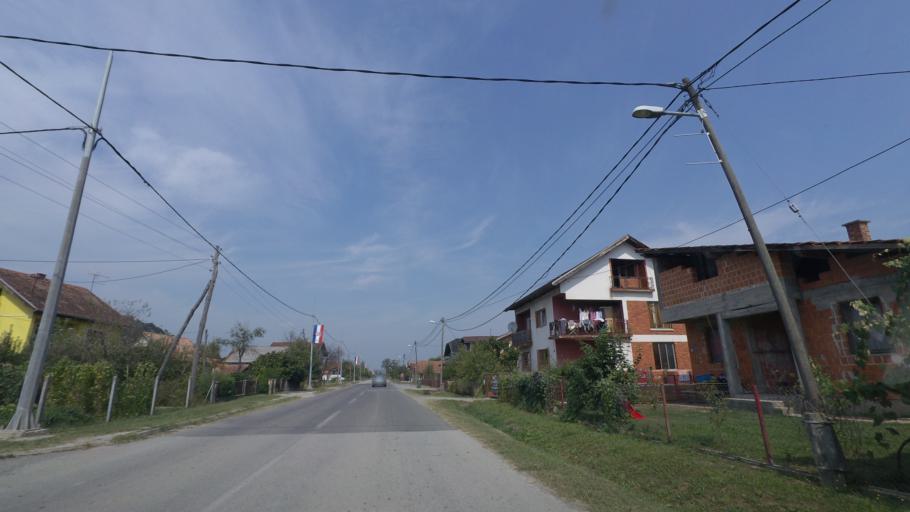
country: HR
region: Sisacko-Moslavacka
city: Glina
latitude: 45.3232
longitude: 16.1070
